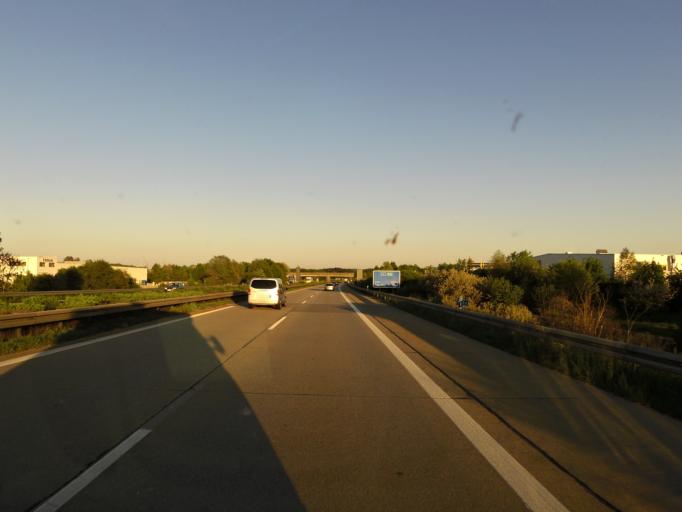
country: DE
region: Bavaria
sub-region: Lower Bavaria
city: Hengersberg
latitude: 48.7657
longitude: 13.0522
